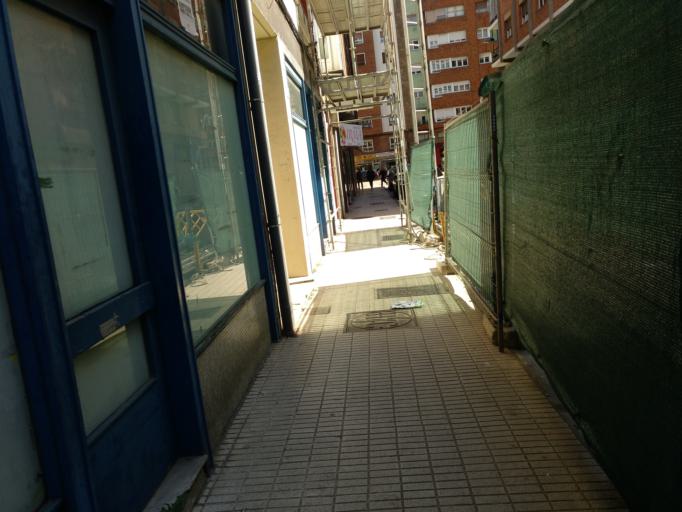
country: ES
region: Asturias
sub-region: Province of Asturias
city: Gijon
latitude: 43.5365
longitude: -5.6673
